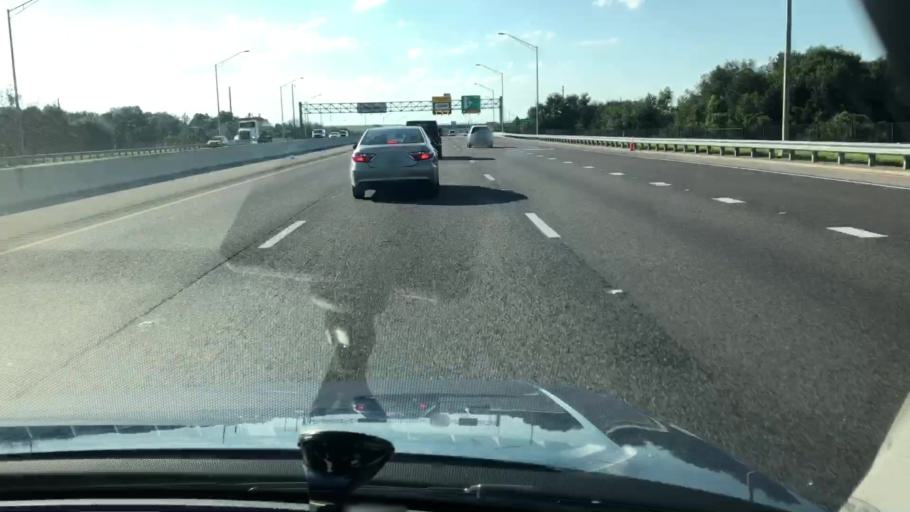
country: US
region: Florida
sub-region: Orange County
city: South Apopka
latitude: 28.6423
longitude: -81.5017
